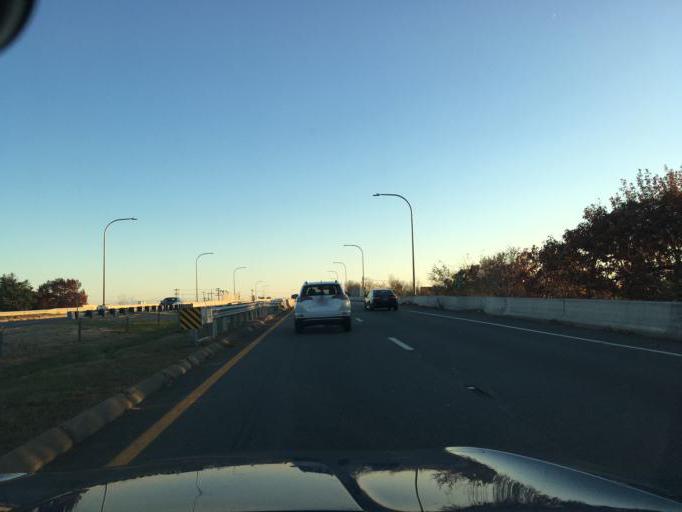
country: US
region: Rhode Island
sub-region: Providence County
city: Cranston
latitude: 41.8051
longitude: -71.4408
